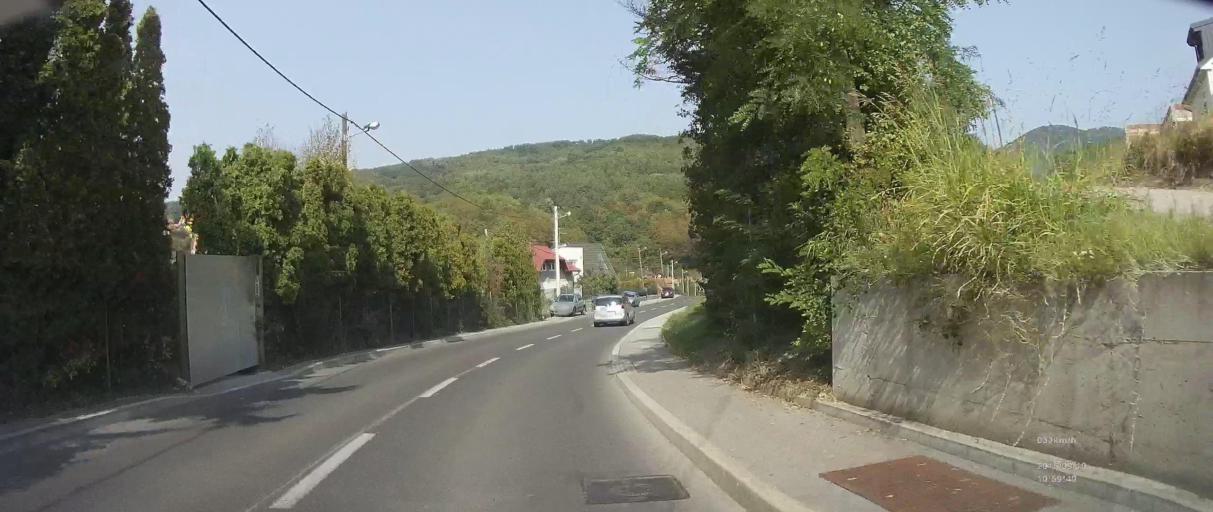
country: HR
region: Grad Zagreb
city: Zagreb
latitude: 45.8505
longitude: 15.9377
